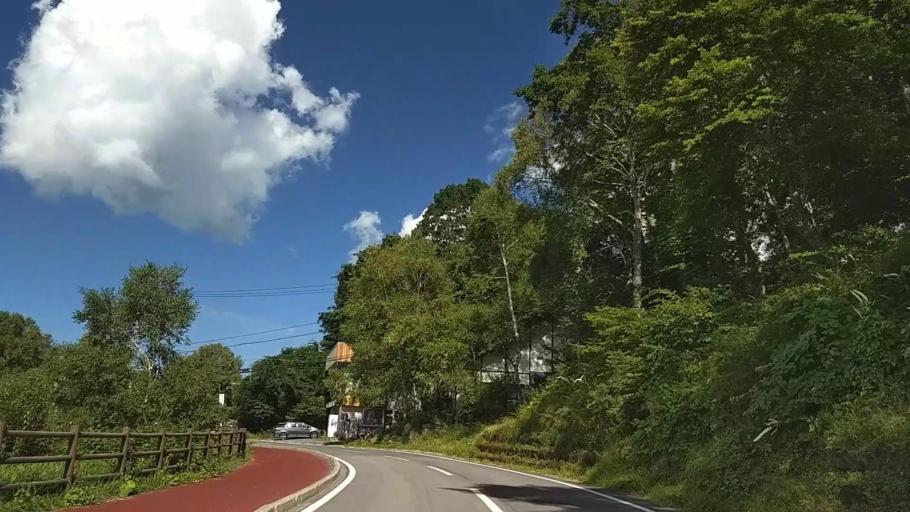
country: JP
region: Nagano
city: Chino
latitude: 36.1027
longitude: 138.2318
